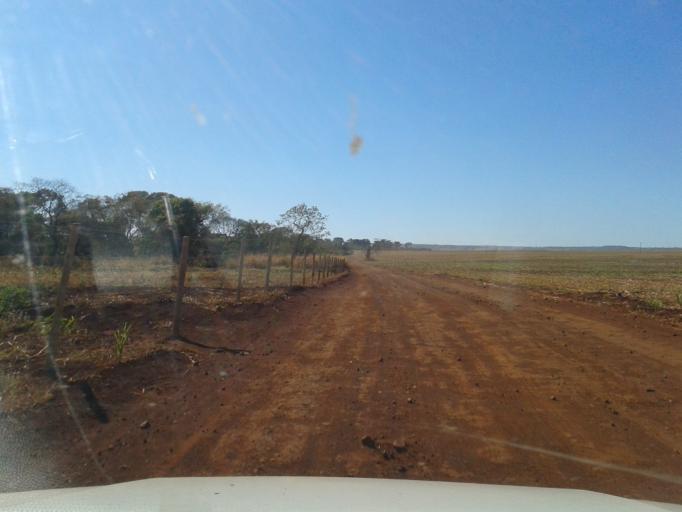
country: BR
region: Minas Gerais
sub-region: Centralina
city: Centralina
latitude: -18.5898
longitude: -49.1579
